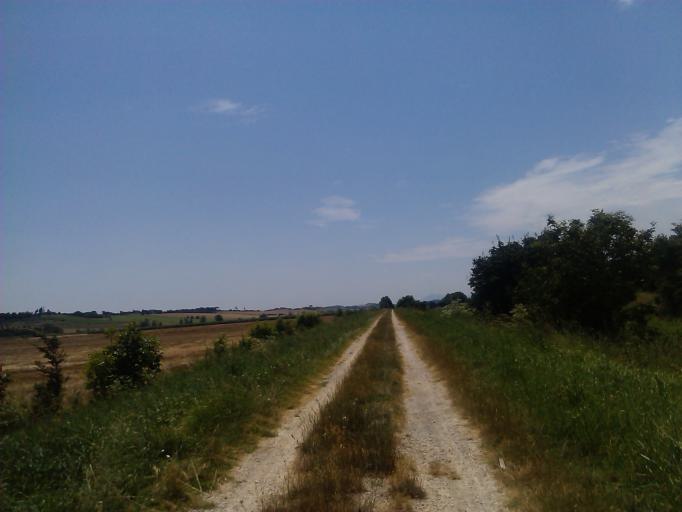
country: IT
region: Tuscany
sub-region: Province of Arezzo
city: Cesa
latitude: 43.3012
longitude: 11.8403
